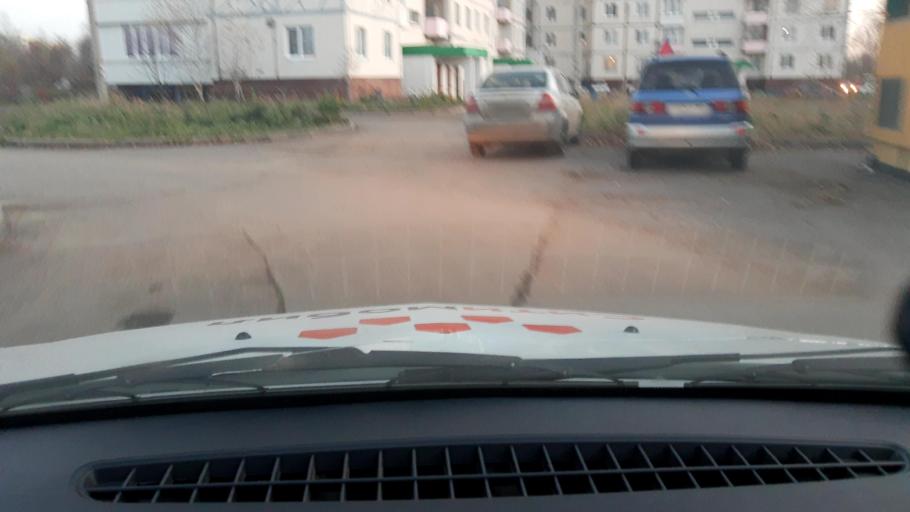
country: RU
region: Bashkortostan
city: Iglino
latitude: 54.7586
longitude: 56.2337
